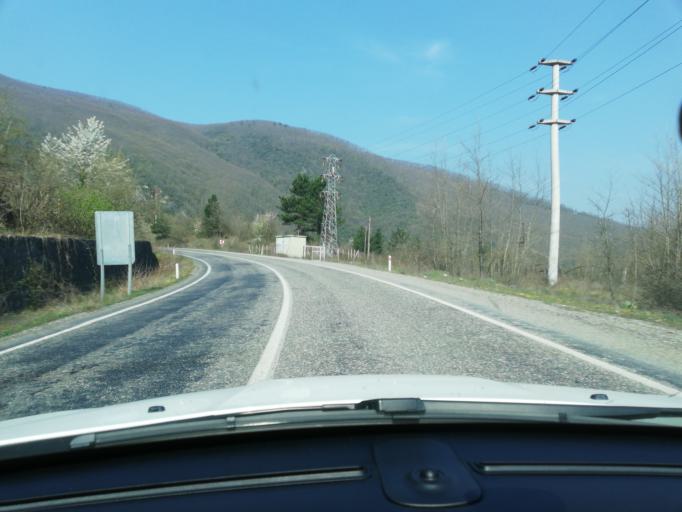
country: TR
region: Karabuk
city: Yenice
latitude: 41.2085
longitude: 32.3625
